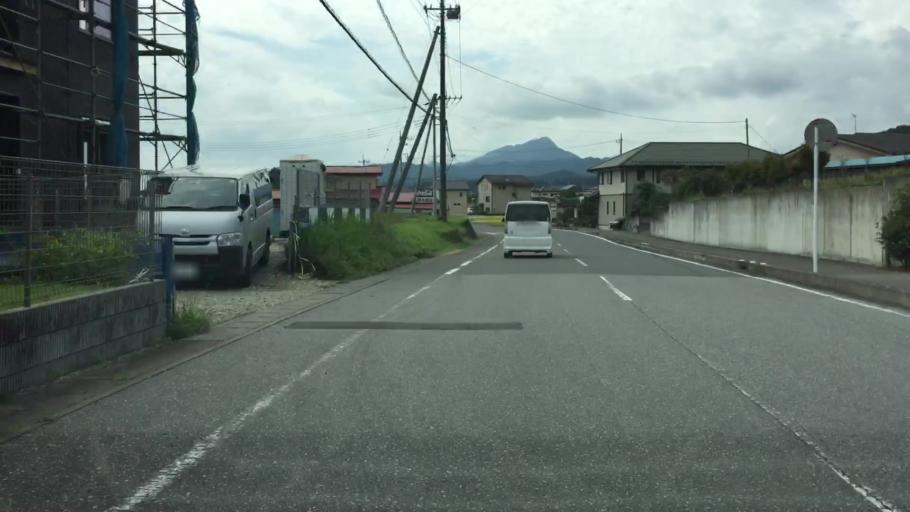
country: JP
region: Tochigi
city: Imaichi
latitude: 36.7453
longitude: 139.6852
